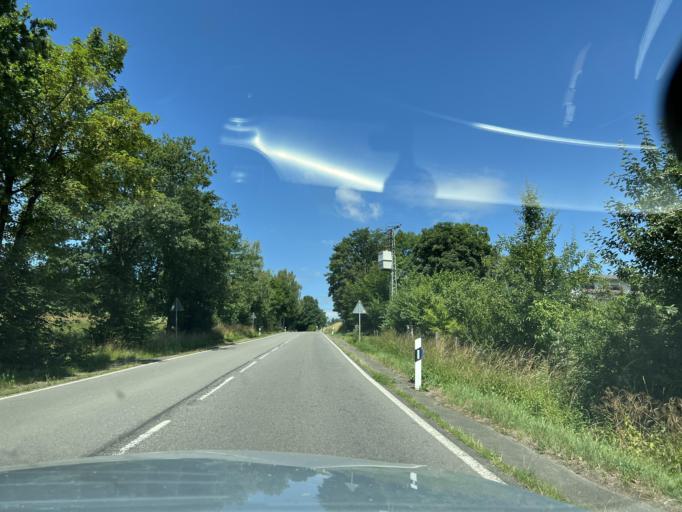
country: DE
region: North Rhine-Westphalia
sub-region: Regierungsbezirk Arnsberg
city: Wenden
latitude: 50.9467
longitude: 7.8840
